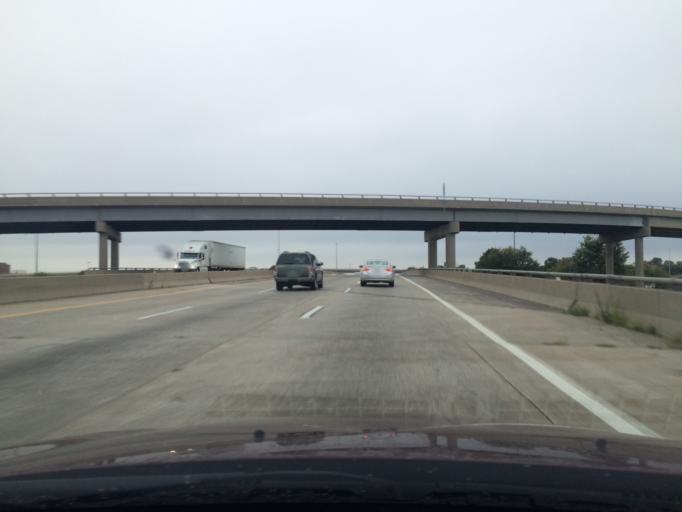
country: US
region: Missouri
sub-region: Saint Louis County
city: Bridgeton
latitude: 38.7495
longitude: -90.4424
